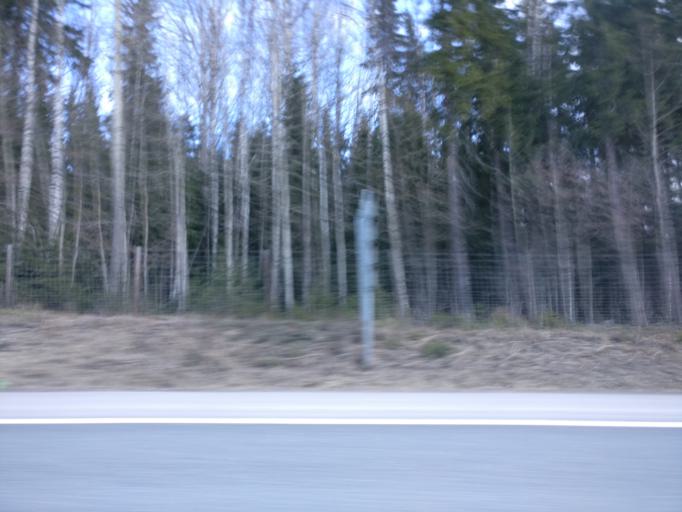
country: FI
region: Haeme
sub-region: Riihimaeki
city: Riihimaeki
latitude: 60.7595
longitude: 24.7267
